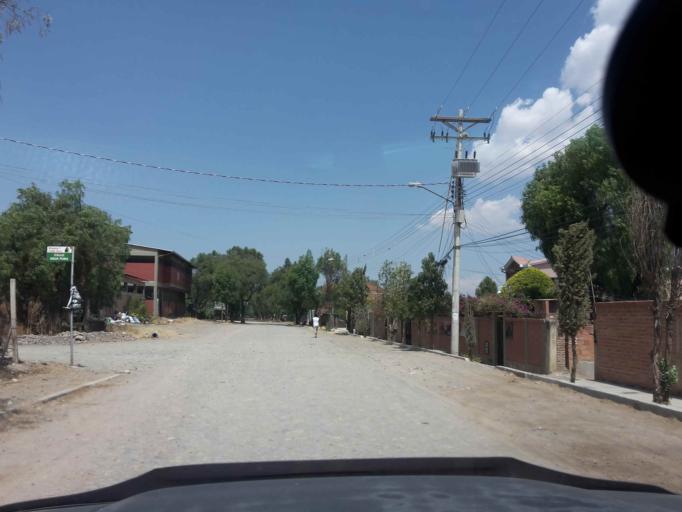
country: BO
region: Cochabamba
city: Cochabamba
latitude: -17.3358
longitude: -66.2154
